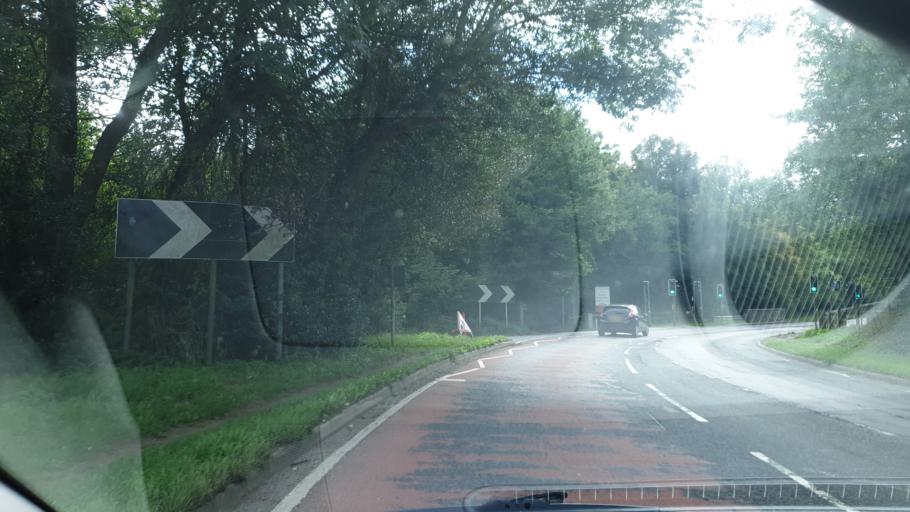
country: GB
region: England
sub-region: East Sussex
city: Forest Row
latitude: 51.1020
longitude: 0.0343
